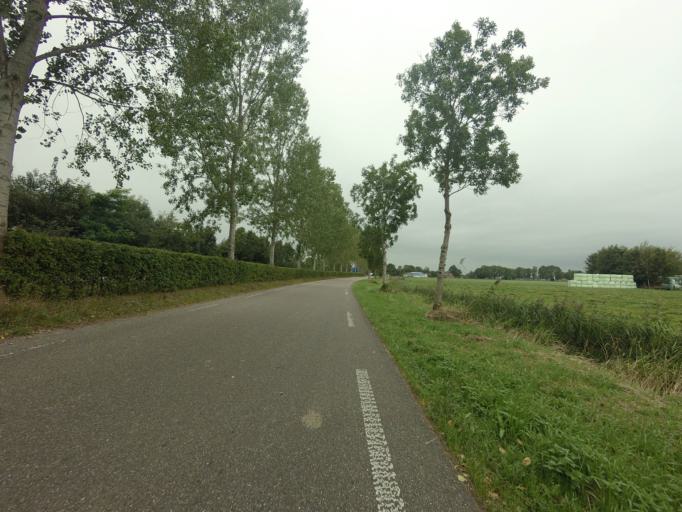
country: NL
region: Friesland
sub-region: Gemeente Opsterland
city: Tijnje
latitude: 53.0165
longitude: 6.0263
